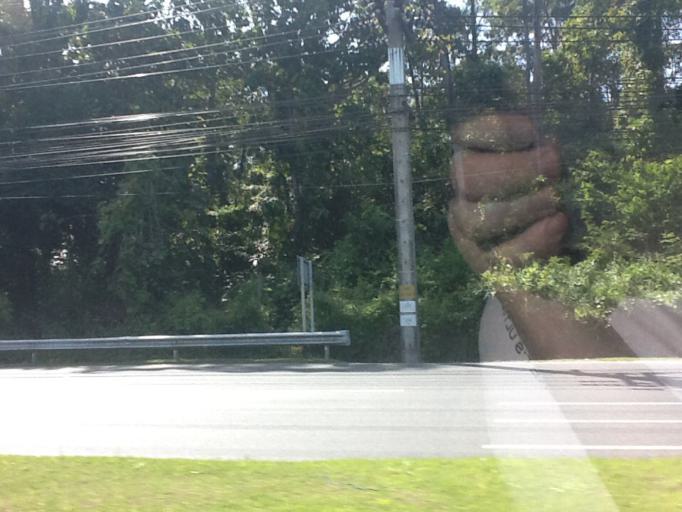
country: TH
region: Phuket
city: Thalang
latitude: 8.0793
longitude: 98.3436
